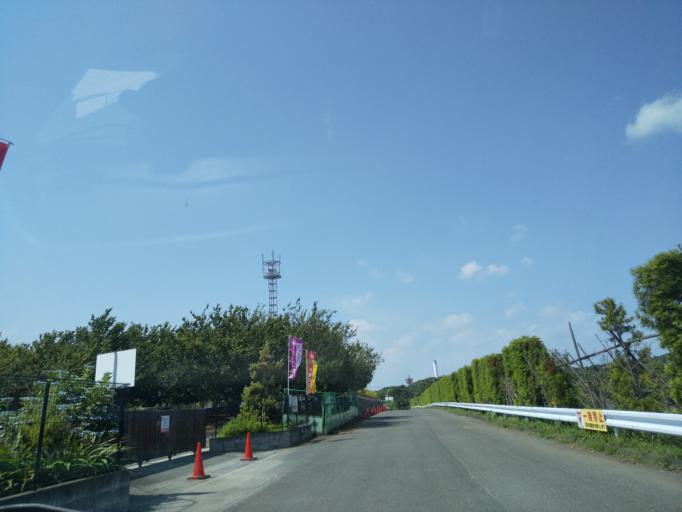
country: JP
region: Kanagawa
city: Zama
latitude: 35.5170
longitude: 139.3897
